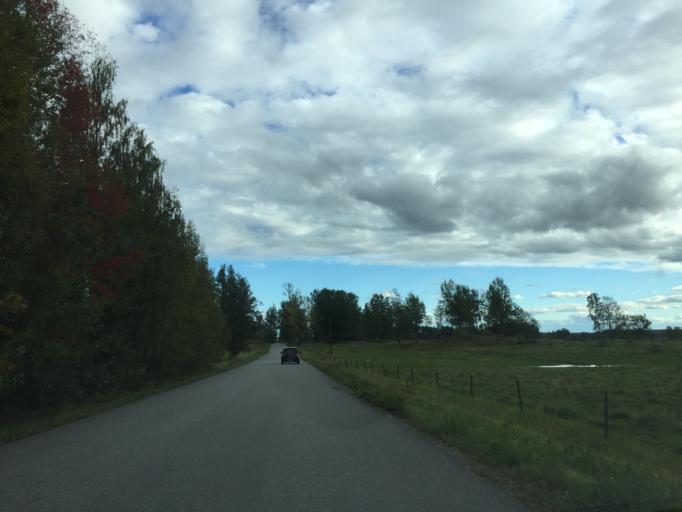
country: SE
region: OErebro
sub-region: Orebro Kommun
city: Hovsta
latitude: 59.3228
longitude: 15.1916
